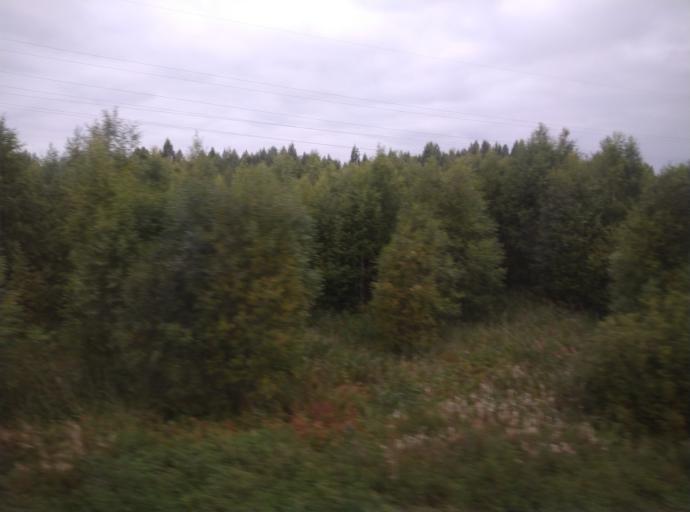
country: RU
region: Kostroma
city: Kosmynino
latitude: 57.5799
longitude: 40.7483
